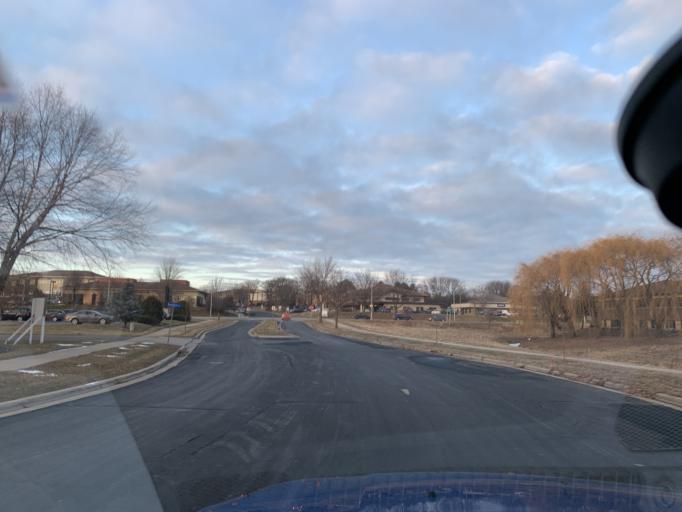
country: US
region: Wisconsin
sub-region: Dane County
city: Madison
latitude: 43.0146
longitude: -89.4285
